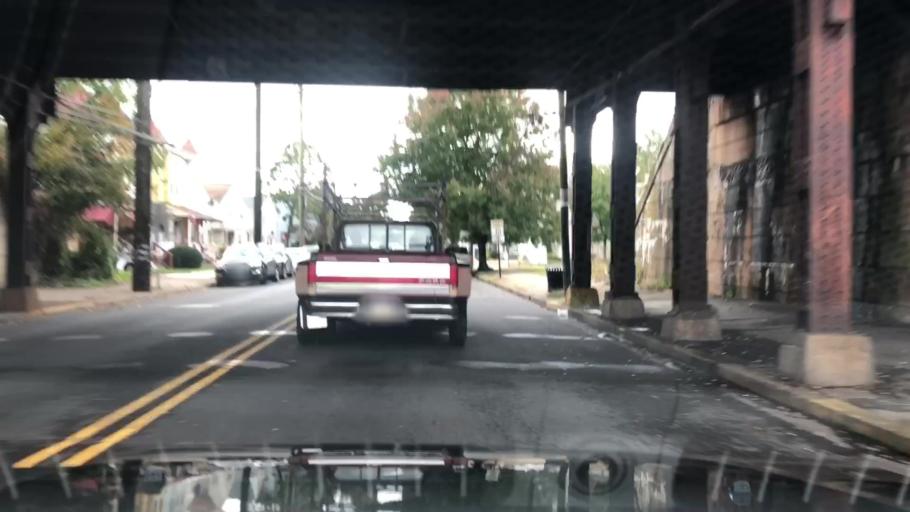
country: US
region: Pennsylvania
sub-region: Bucks County
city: Bristol
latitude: 40.1012
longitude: -74.8629
